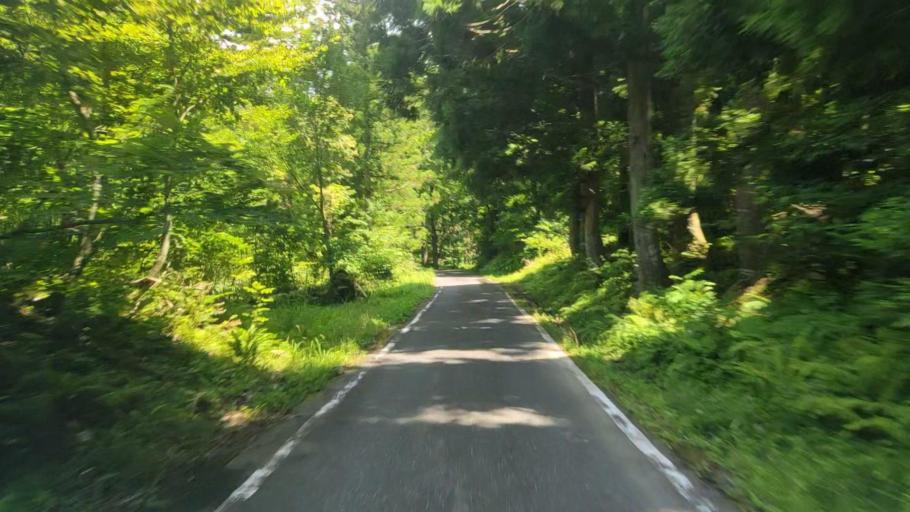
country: JP
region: Fukui
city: Ono
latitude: 35.7647
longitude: 136.5531
